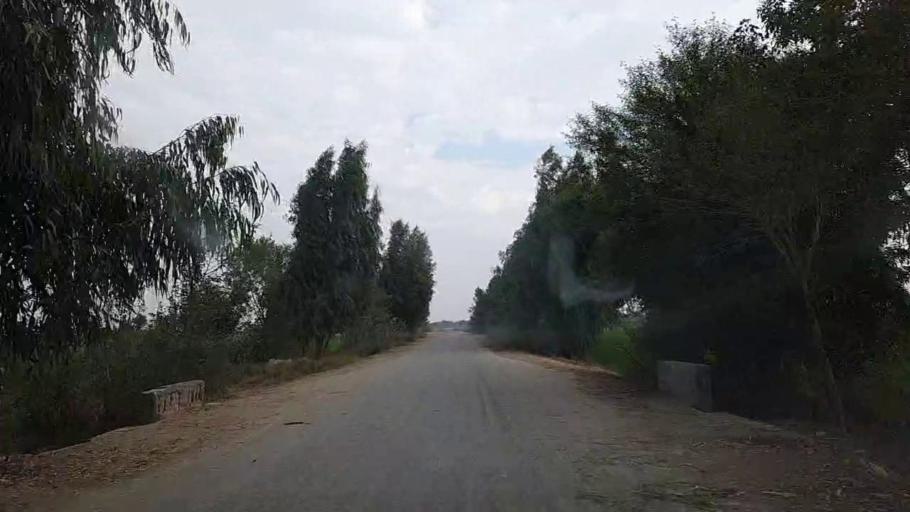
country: PK
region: Sindh
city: Sanghar
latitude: 26.2269
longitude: 69.0235
